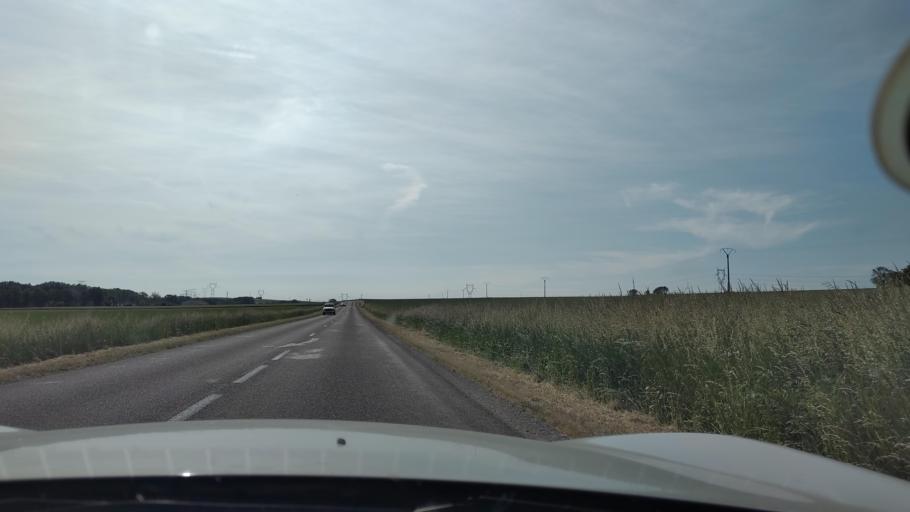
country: FR
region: Champagne-Ardenne
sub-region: Departement de l'Aube
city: Nogent-sur-Seine
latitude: 48.4644
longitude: 3.5786
